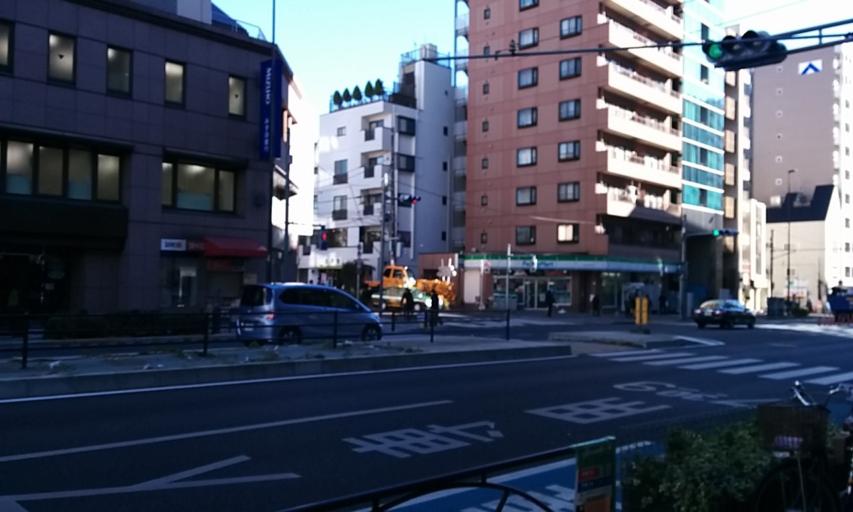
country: JP
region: Tokyo
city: Tokyo
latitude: 35.7168
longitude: 139.7381
